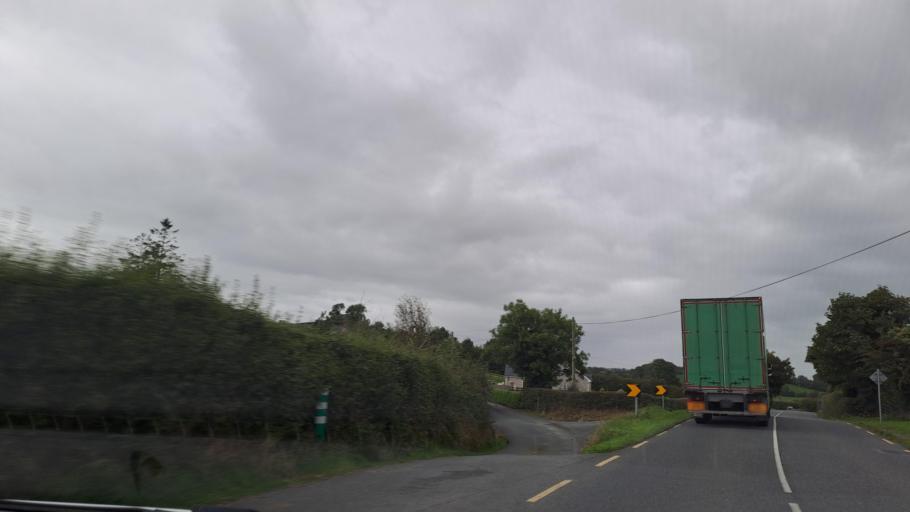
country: IE
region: Ulster
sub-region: County Monaghan
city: Monaghan
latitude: 54.1361
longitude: -6.9113
